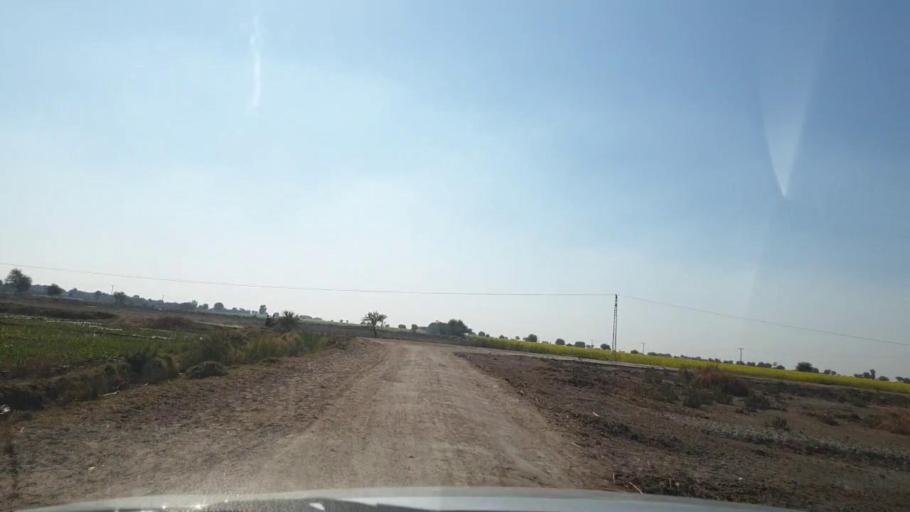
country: PK
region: Sindh
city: Jhol
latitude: 25.8070
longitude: 69.0356
